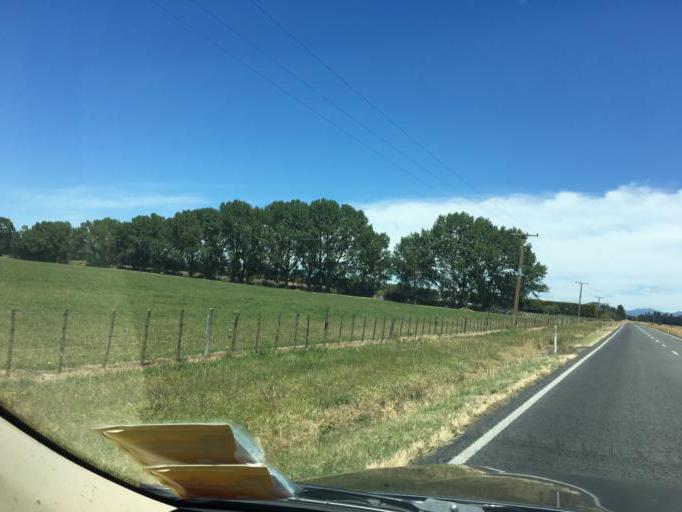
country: NZ
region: Hawke's Bay
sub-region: Hastings District
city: Hastings
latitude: -39.9969
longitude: 176.4179
